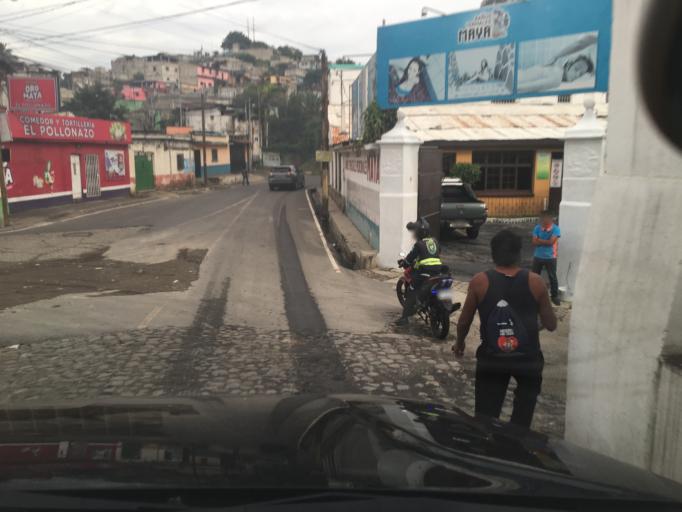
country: GT
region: Guatemala
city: Amatitlan
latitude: 14.4812
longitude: -90.6153
